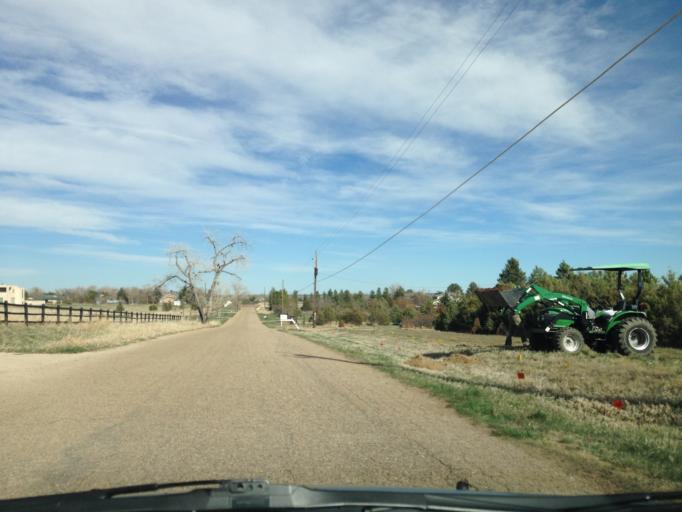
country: US
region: Colorado
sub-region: Boulder County
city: Gunbarrel
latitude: 40.0619
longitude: -105.1253
